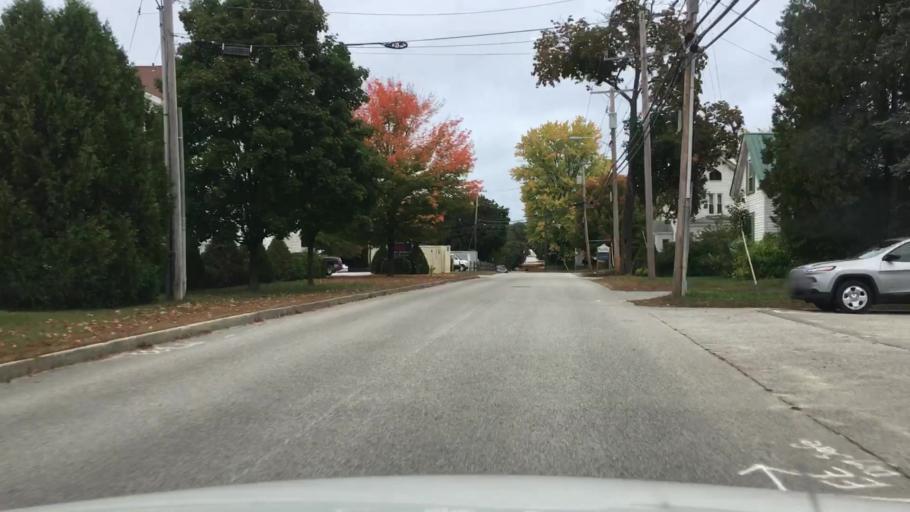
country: US
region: Maine
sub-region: Oxford County
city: Norway
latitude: 44.2107
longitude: -70.5318
